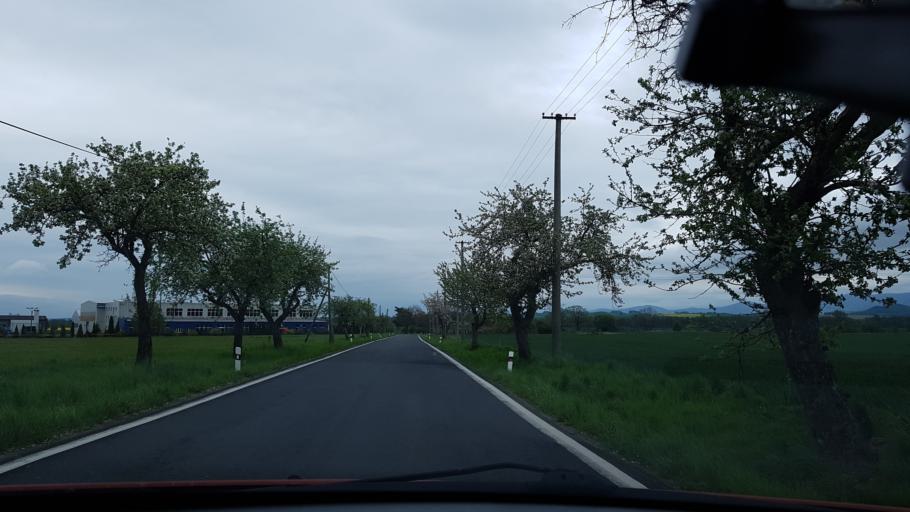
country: CZ
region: Olomoucky
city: Javornik
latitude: 50.3926
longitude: 17.0162
